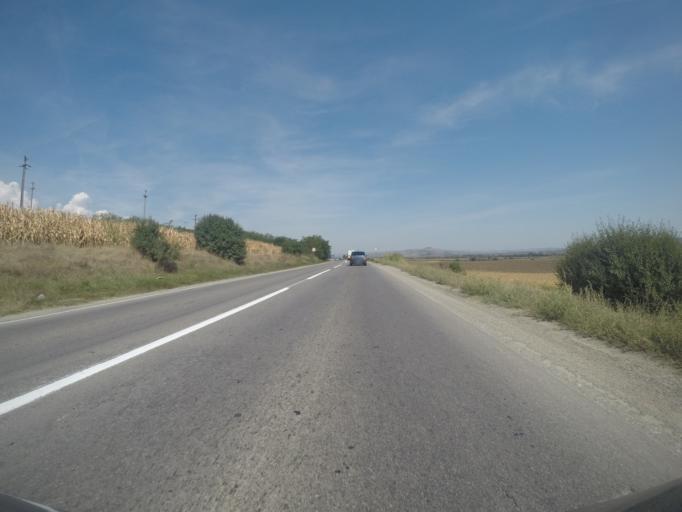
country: RO
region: Alba
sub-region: Comuna Santimbru
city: Santimbru
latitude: 46.1439
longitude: 23.6432
